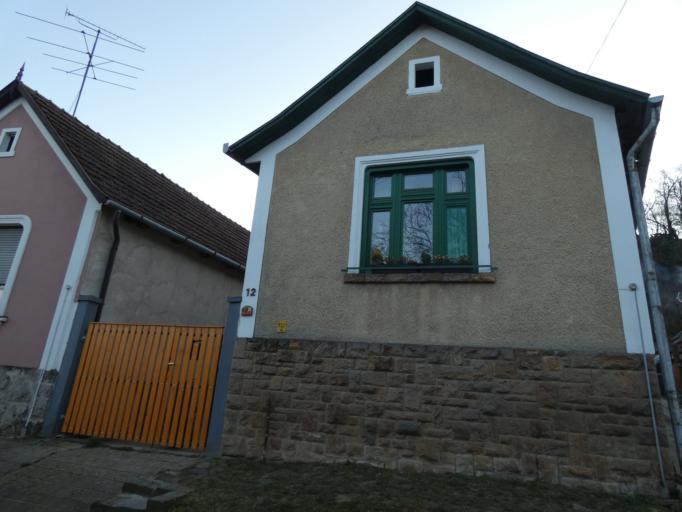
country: HU
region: Pest
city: Nagymaros
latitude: 47.7914
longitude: 18.9563
